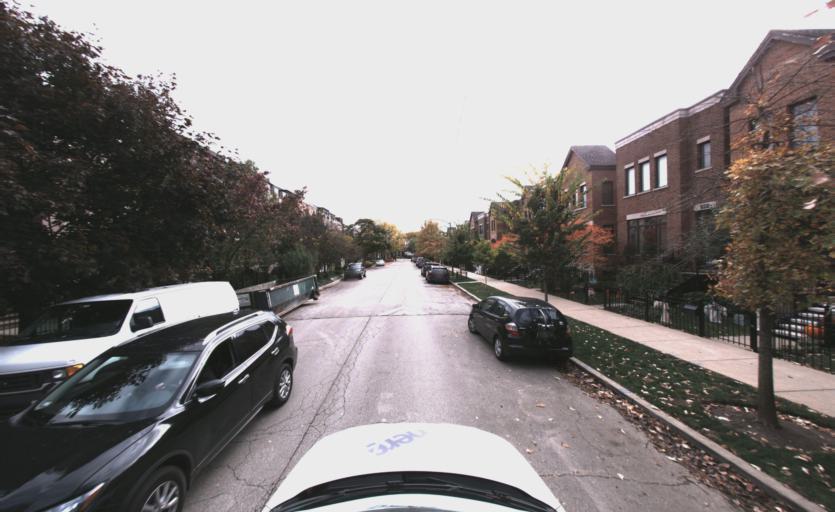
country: US
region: Illinois
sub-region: Cook County
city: Chicago
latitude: 41.9301
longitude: -87.6708
